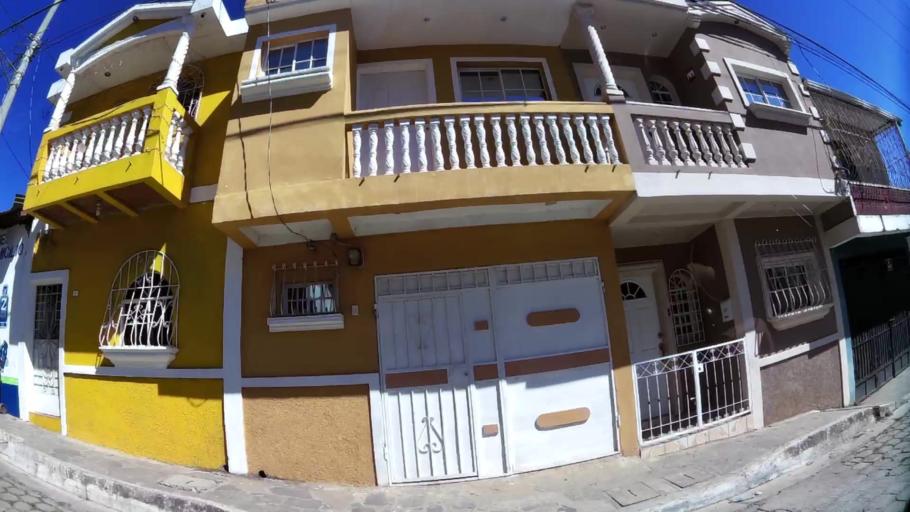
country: SV
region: Ahuachapan
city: Concepcion de Ataco
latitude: 13.8673
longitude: -89.8516
